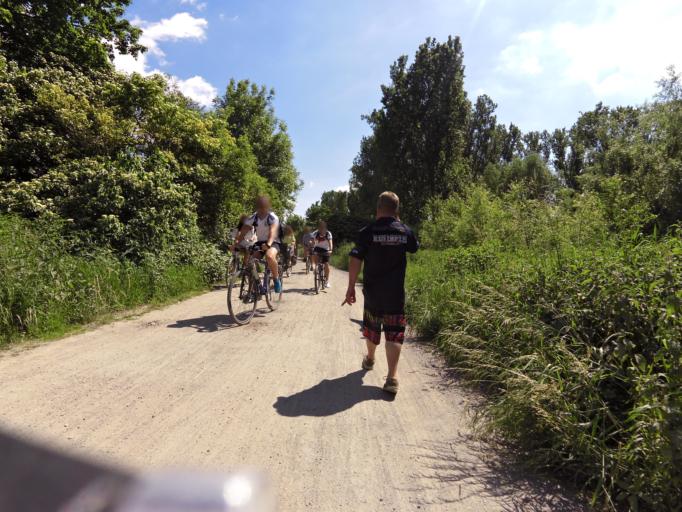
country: DE
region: Rheinland-Pfalz
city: Nackenheim
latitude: 49.9340
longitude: 8.3511
